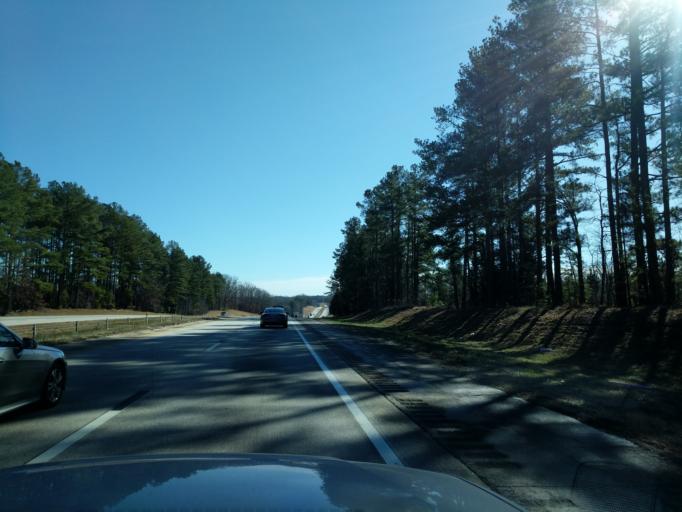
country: US
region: South Carolina
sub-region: Laurens County
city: Watts Mills
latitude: 34.5275
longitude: -81.9232
